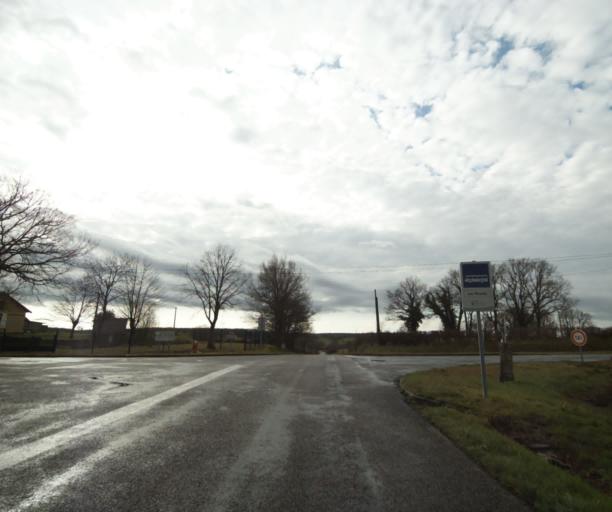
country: FR
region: Auvergne
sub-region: Departement de l'Allier
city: Toulon-sur-Allier
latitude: 46.5297
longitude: 3.4081
